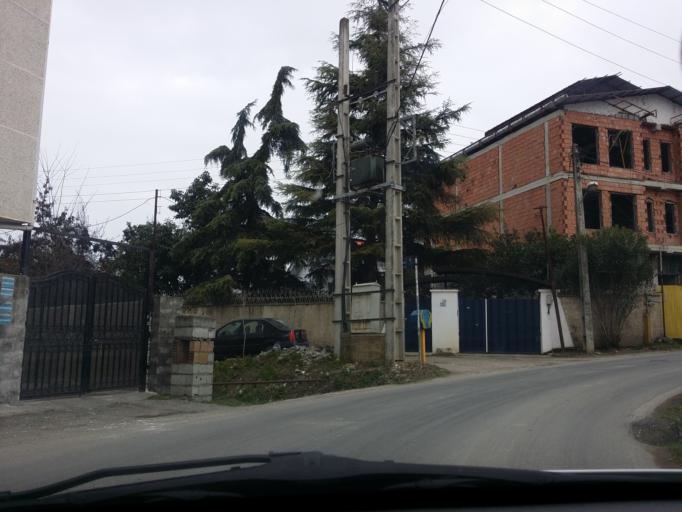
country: IR
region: Mazandaran
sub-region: Nowshahr
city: Nowshahr
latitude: 36.6453
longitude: 51.4817
